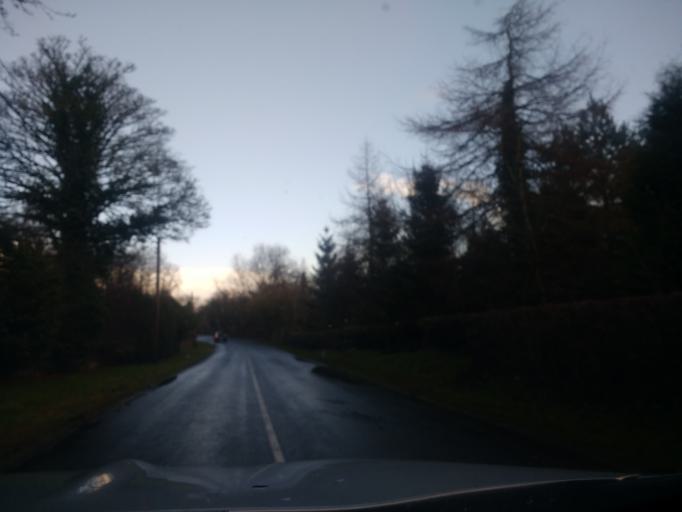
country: IE
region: Ulster
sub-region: County Donegal
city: Ramelton
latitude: 55.0459
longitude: -7.6438
